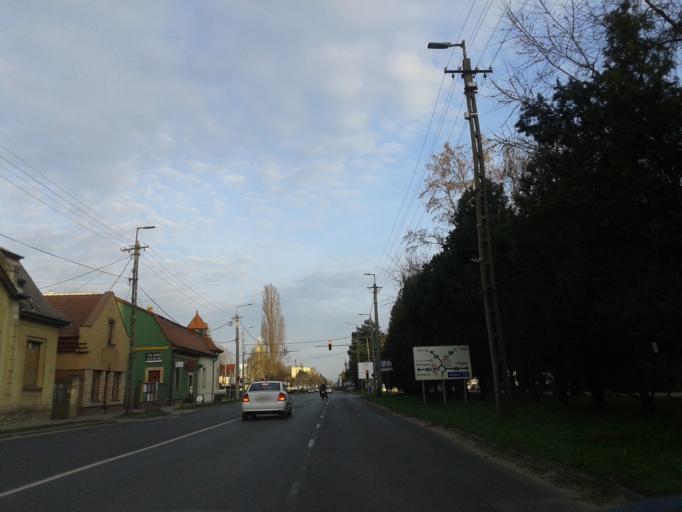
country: HU
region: Komarom-Esztergom
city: Komarom
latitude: 47.7445
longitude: 18.1158
